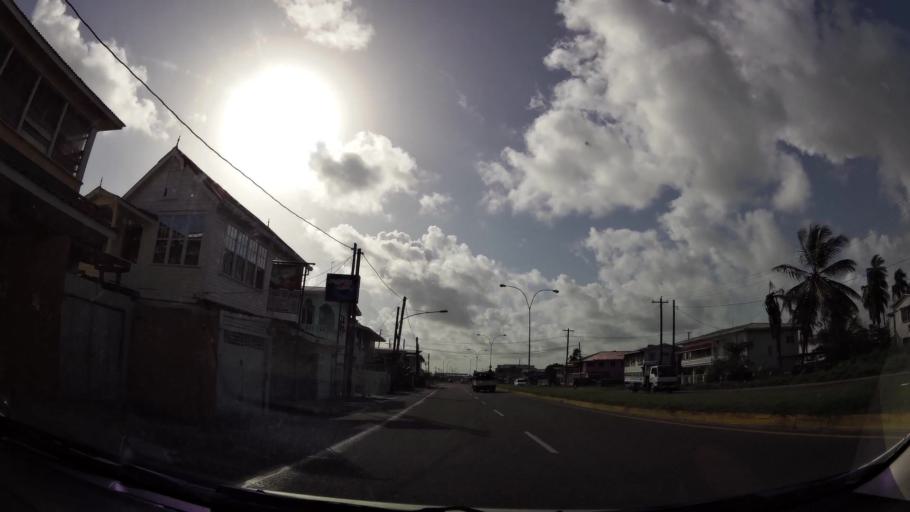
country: GY
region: Demerara-Mahaica
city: Georgetown
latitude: 6.8193
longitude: -58.0912
